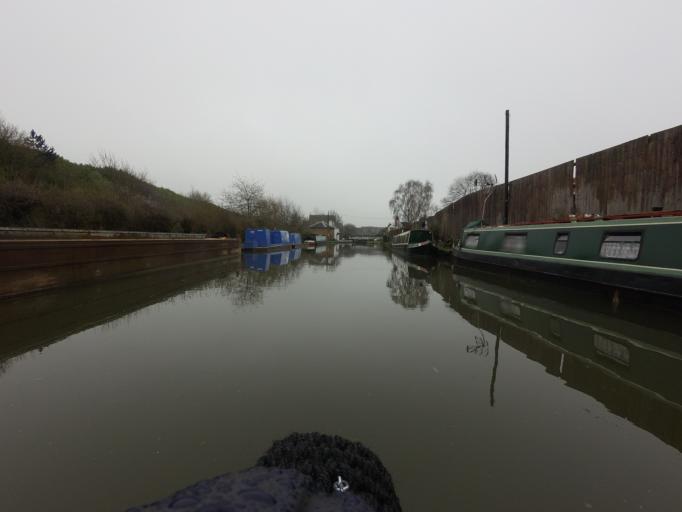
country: GB
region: England
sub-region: Milton Keynes
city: Water Eaton
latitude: 52.0018
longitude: -0.7147
